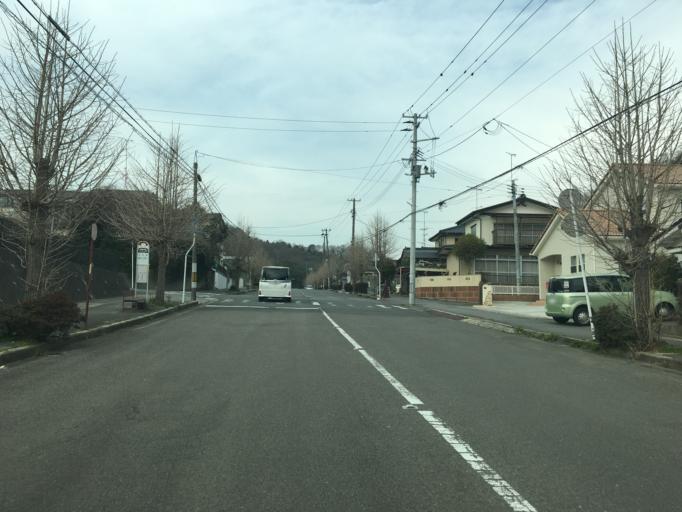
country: JP
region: Fukushima
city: Iwaki
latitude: 36.9876
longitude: 140.8858
